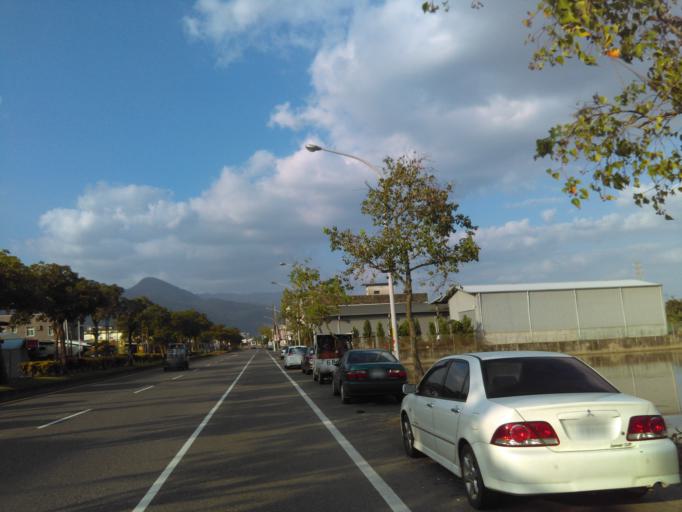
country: TW
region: Taiwan
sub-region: Yilan
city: Yilan
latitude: 24.7990
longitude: 121.7644
